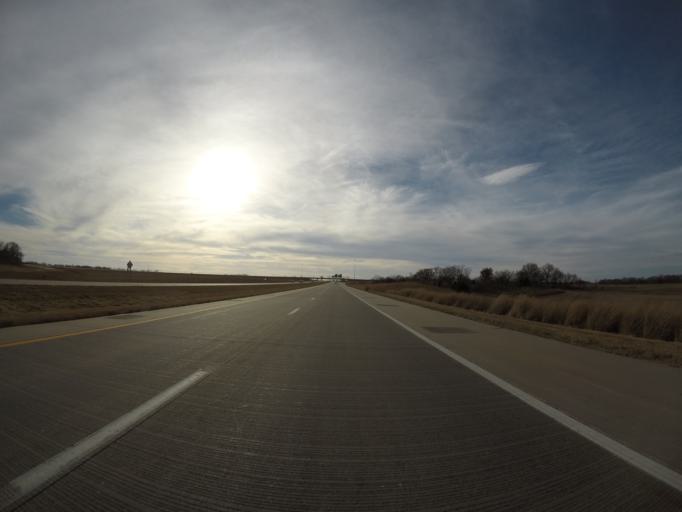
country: US
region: Kansas
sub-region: Franklin County
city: Ottawa
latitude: 38.6410
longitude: -95.2149
